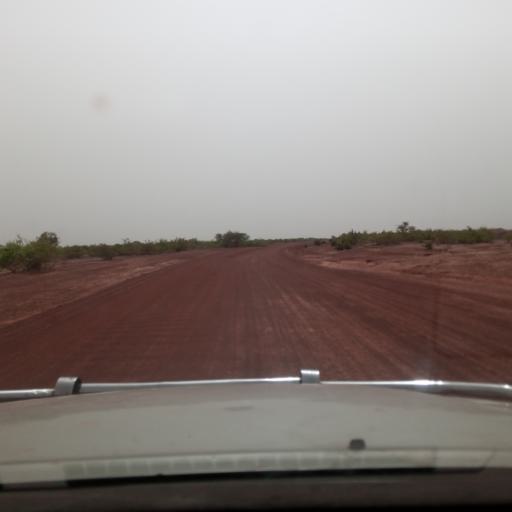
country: ML
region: Koulikoro
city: Banamba
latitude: 13.3335
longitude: -7.5330
